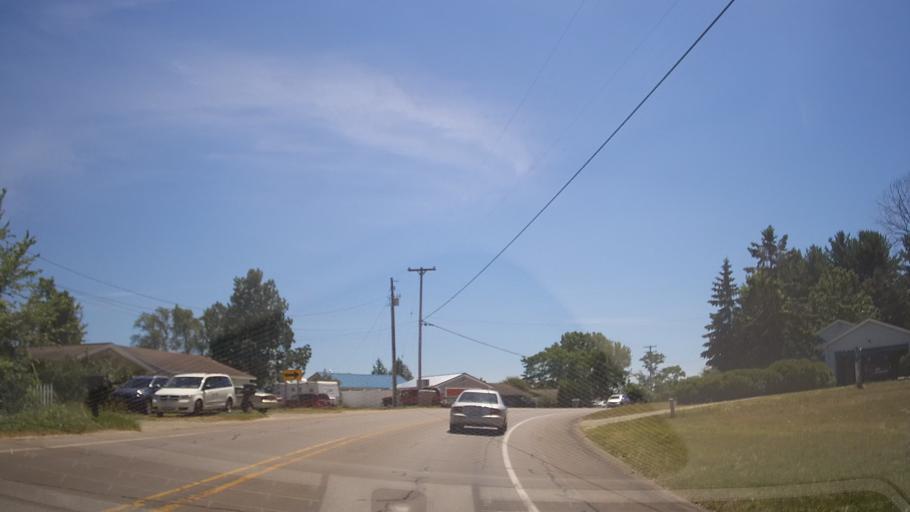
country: US
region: Michigan
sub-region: Grand Traverse County
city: Traverse City
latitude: 44.7016
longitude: -85.6911
